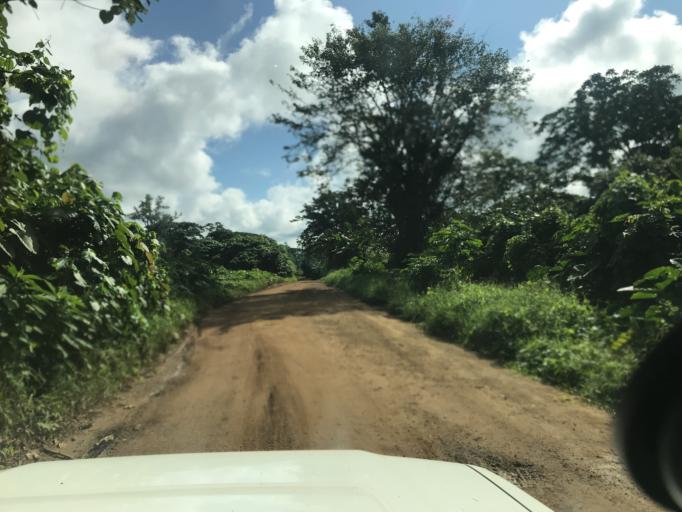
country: VU
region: Sanma
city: Luganville
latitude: -15.4845
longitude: 167.0895
